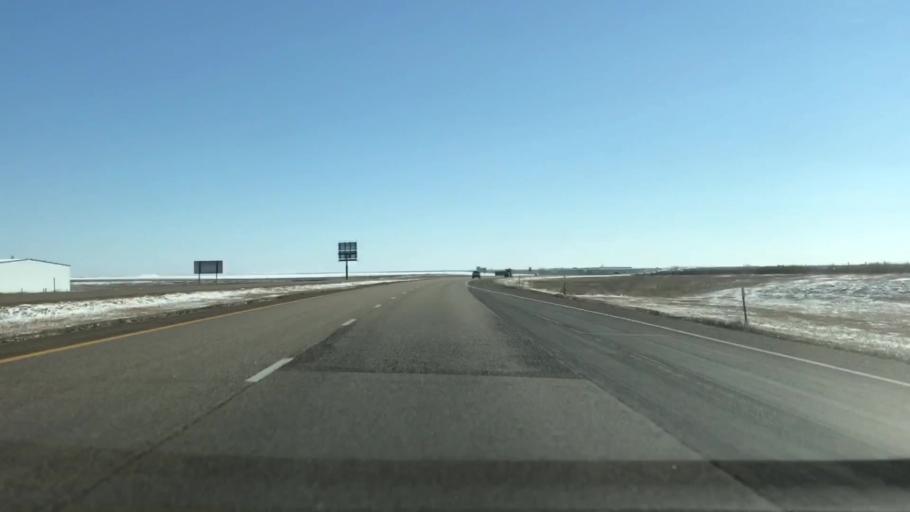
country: US
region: Kansas
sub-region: Thomas County
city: Colby
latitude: 39.3614
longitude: -101.0314
